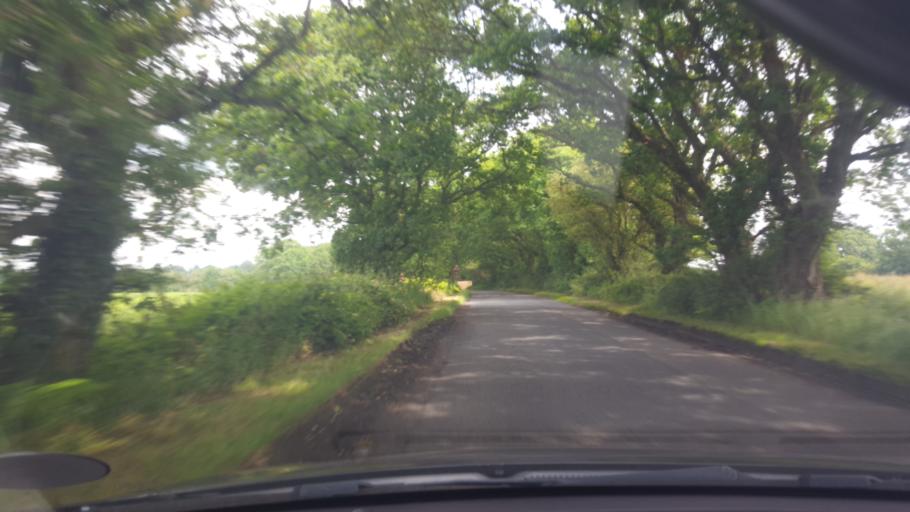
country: GB
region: England
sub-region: Essex
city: Great Bentley
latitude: 51.8712
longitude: 1.0795
